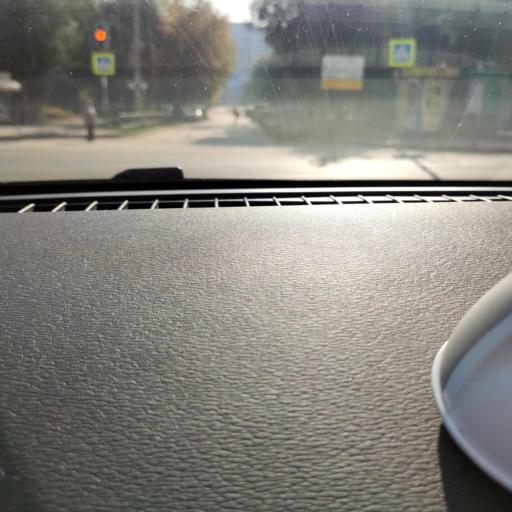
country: RU
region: Samara
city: Samara
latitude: 53.1970
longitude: 50.2206
